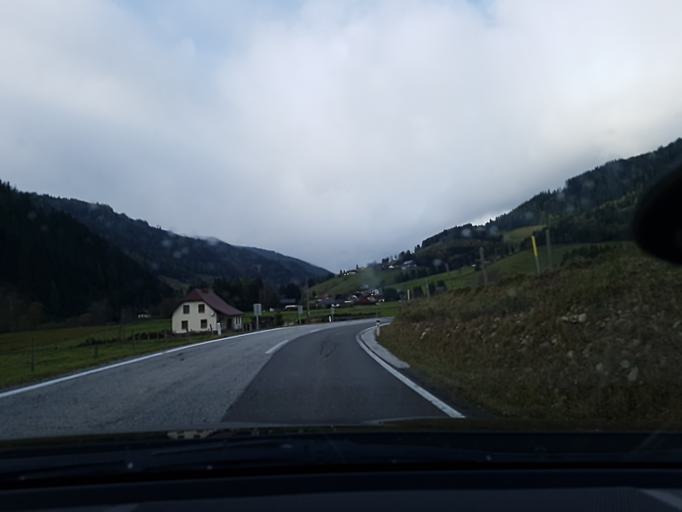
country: AT
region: Styria
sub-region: Politischer Bezirk Murtal
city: Sankt Johann am Tauern
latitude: 47.3141
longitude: 14.4822
